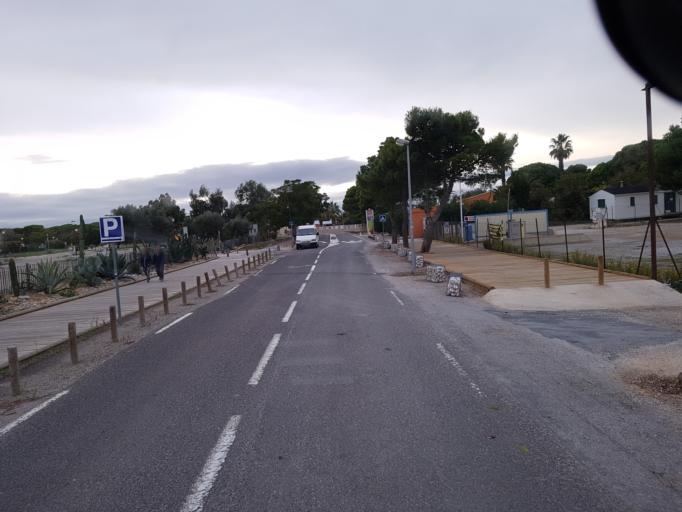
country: FR
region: Languedoc-Roussillon
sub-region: Departement des Pyrenees-Orientales
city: Le Barcares
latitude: 42.7674
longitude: 3.0309
